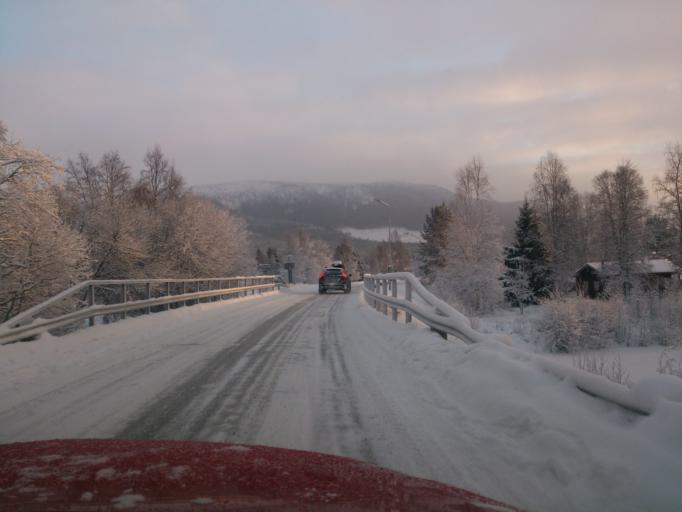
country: SE
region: Jaemtland
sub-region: Harjedalens Kommun
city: Sveg
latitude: 62.4442
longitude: 13.8701
